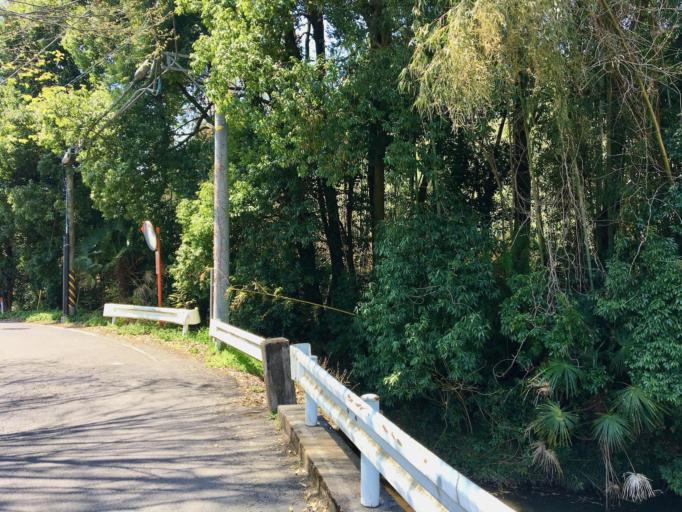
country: JP
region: Saitama
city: Sakado
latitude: 35.9030
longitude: 139.3602
